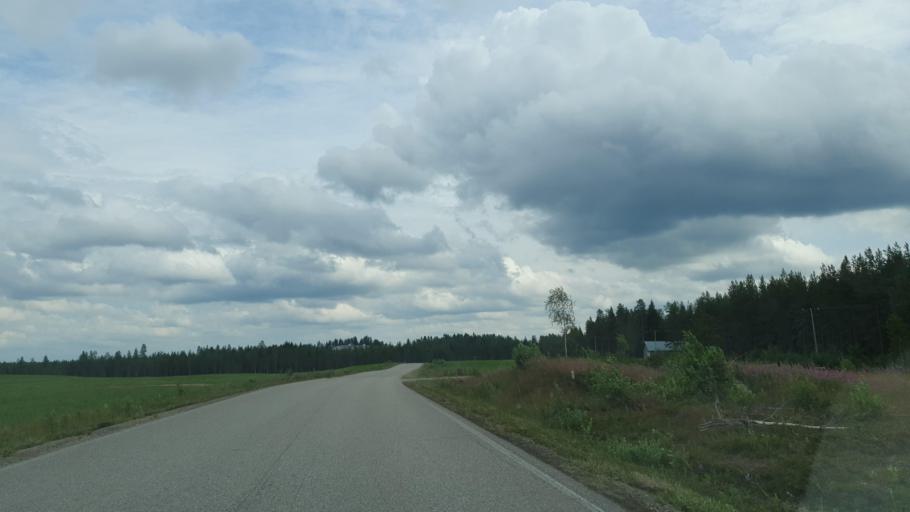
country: FI
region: Kainuu
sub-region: Kehys-Kainuu
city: Kuhmo
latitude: 64.6022
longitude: 29.7733
